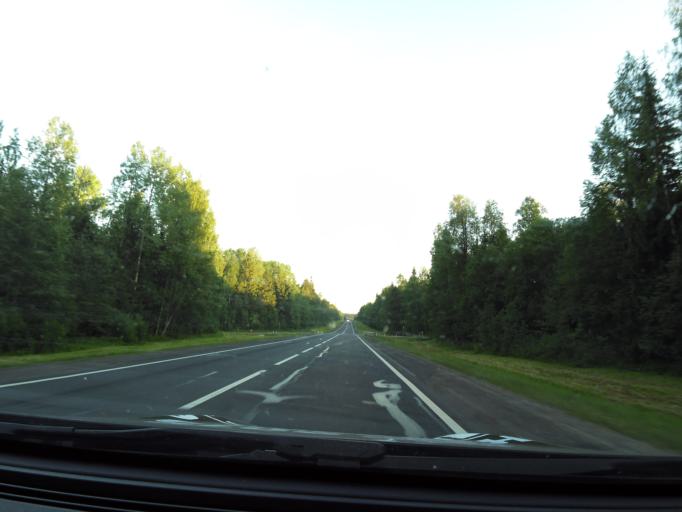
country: RU
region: Jaroslavl
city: Prechistoye
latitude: 58.5221
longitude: 40.3477
